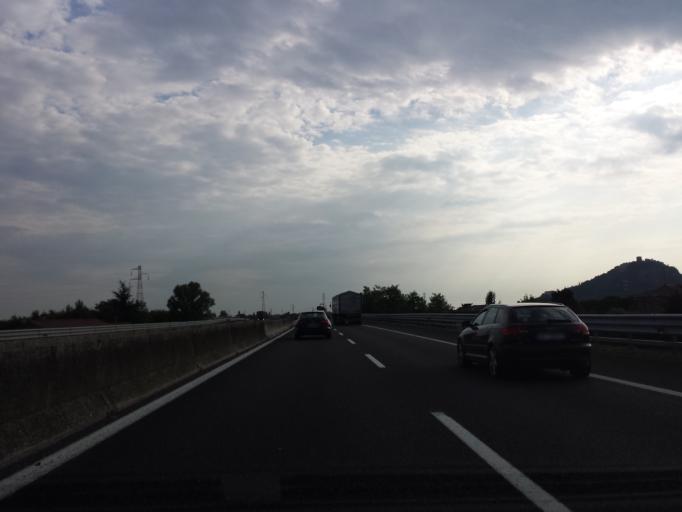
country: IT
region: Veneto
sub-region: Provincia di Padova
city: Pernumia
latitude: 45.2555
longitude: 11.7759
